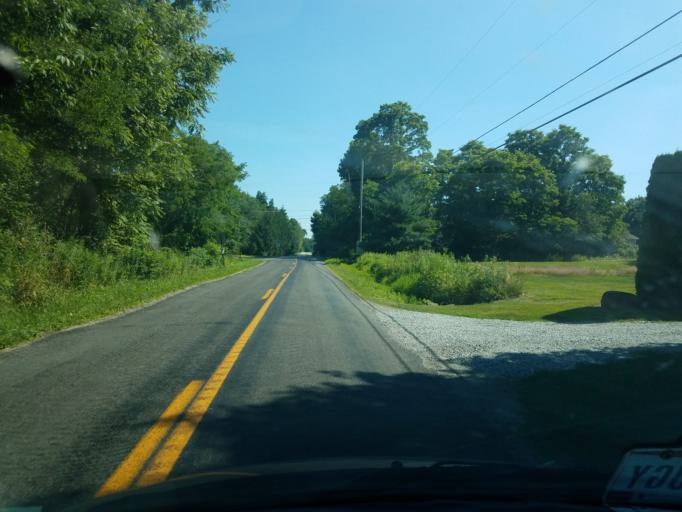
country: US
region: Ohio
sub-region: Portage County
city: Mantua
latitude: 41.3249
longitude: -81.2012
